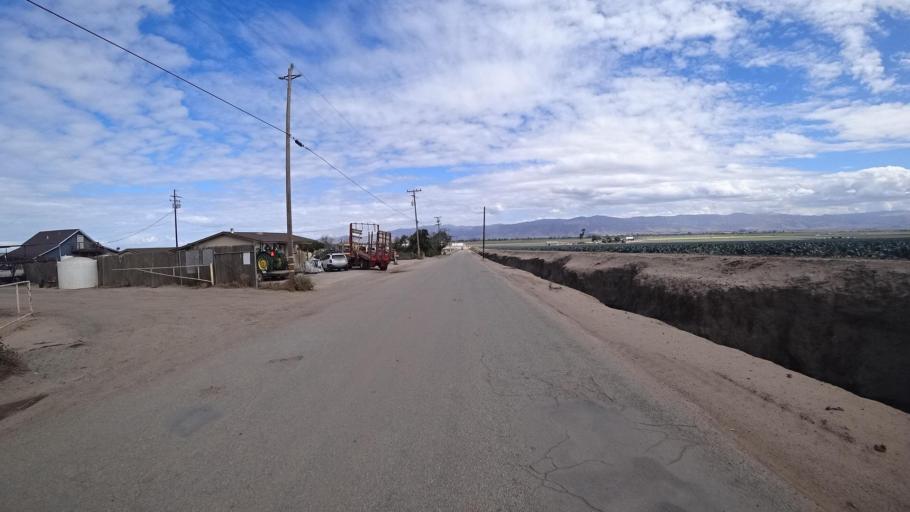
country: US
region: California
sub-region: Monterey County
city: Chualar
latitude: 36.5926
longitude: -121.6033
